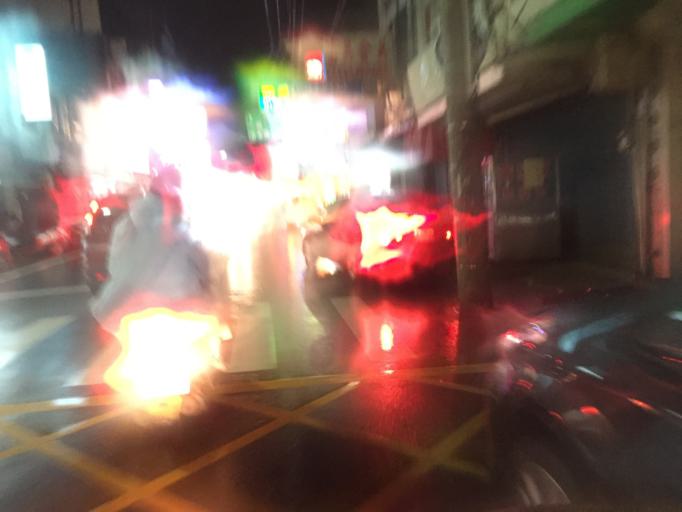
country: TW
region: Taiwan
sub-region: Hsinchu
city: Hsinchu
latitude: 24.8153
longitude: 120.9677
